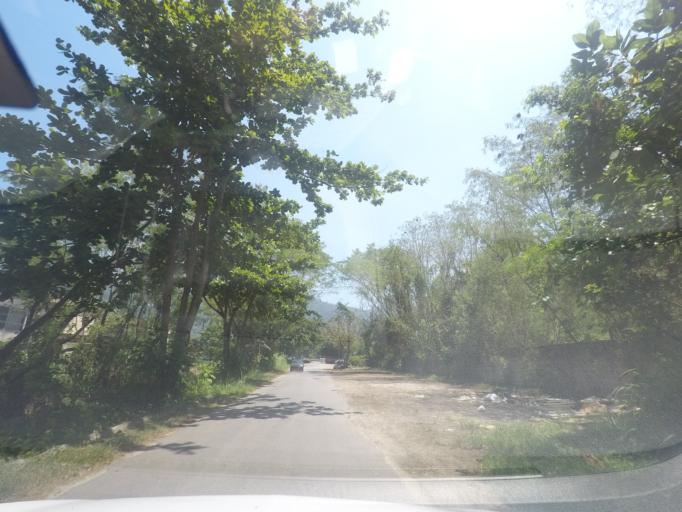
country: BR
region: Rio de Janeiro
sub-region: Nilopolis
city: Nilopolis
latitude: -22.9899
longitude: -43.4556
